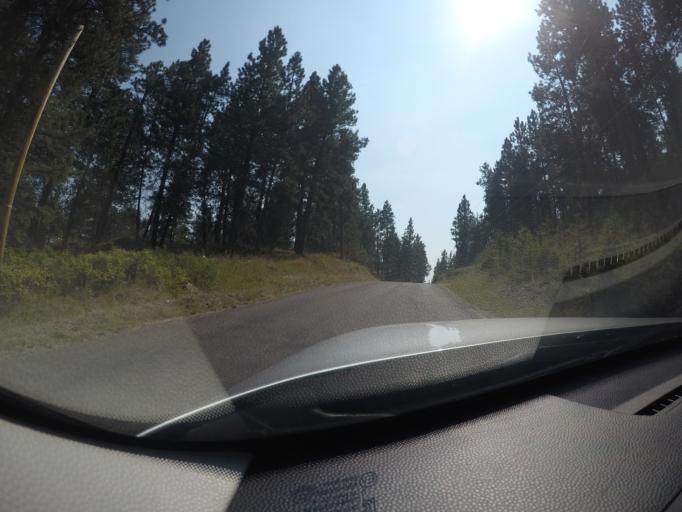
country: US
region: Montana
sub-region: Lake County
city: Polson
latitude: 47.7674
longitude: -114.1520
